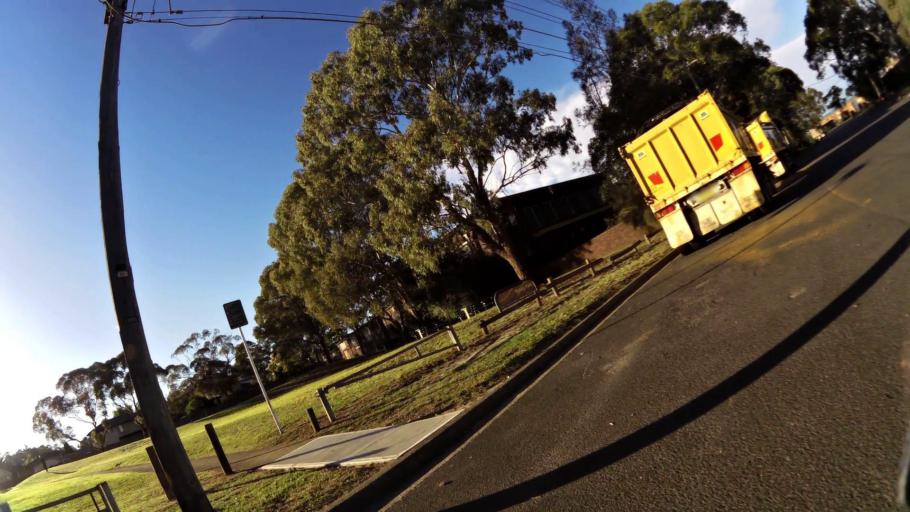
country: AU
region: New South Wales
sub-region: Bankstown
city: Milperra
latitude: -33.9220
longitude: 150.9995
